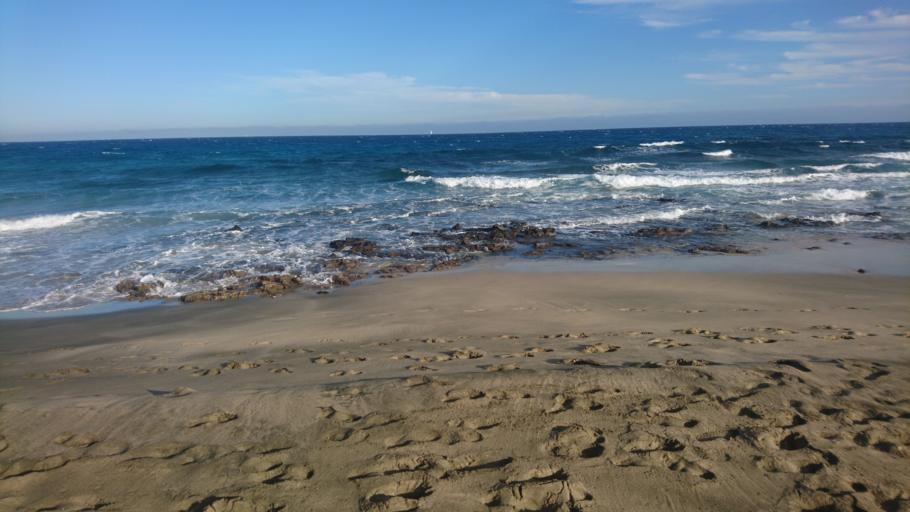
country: ES
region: Canary Islands
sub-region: Provincia de Las Palmas
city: Playa Blanca
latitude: 28.8406
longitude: -13.7854
